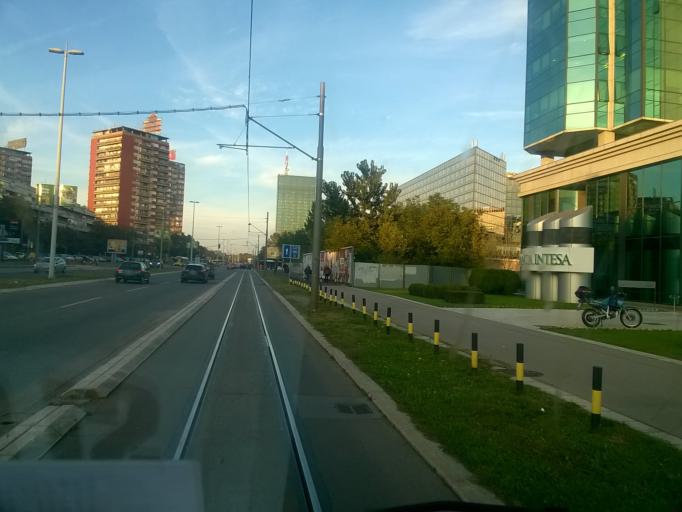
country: RS
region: Central Serbia
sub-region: Belgrade
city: Novi Beograd
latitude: 44.8118
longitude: 20.4321
